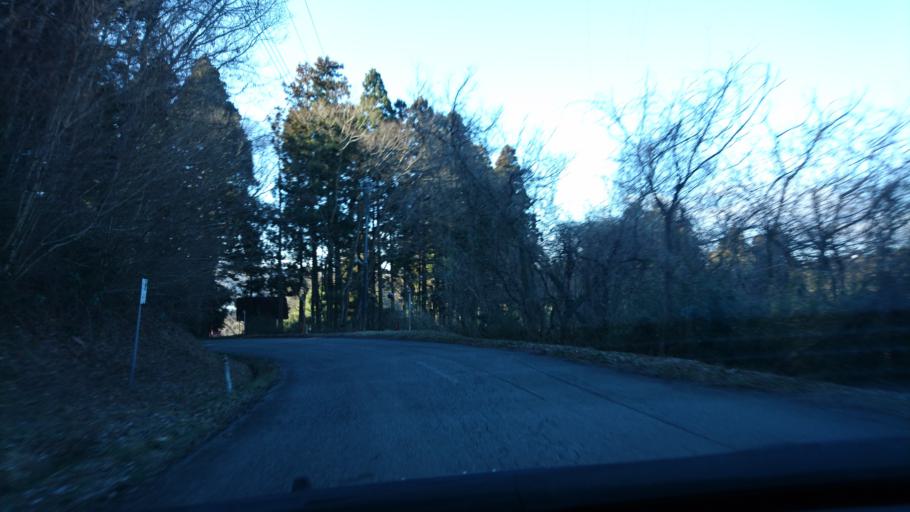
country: JP
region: Iwate
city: Ichinoseki
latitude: 38.8715
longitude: 141.2947
